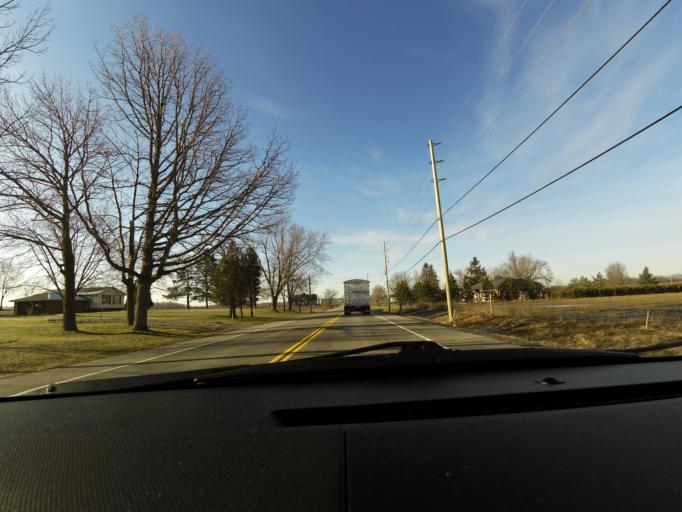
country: CA
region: Ontario
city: Ancaster
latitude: 43.0757
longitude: -79.9240
